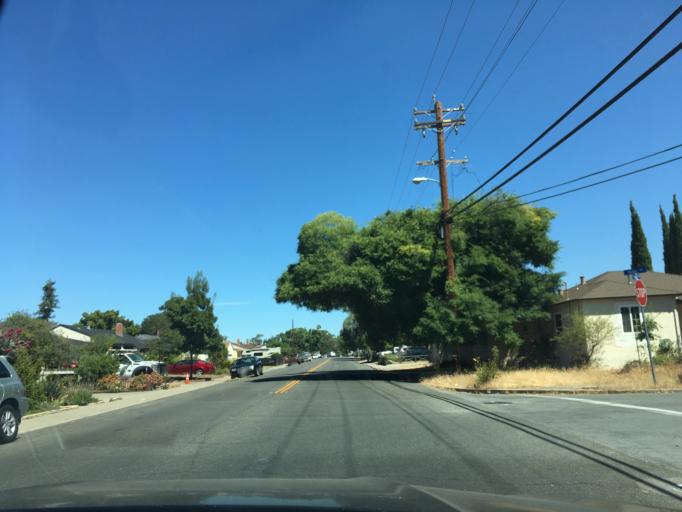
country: US
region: California
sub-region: Santa Clara County
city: East Foothills
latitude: 37.3875
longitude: -121.8307
